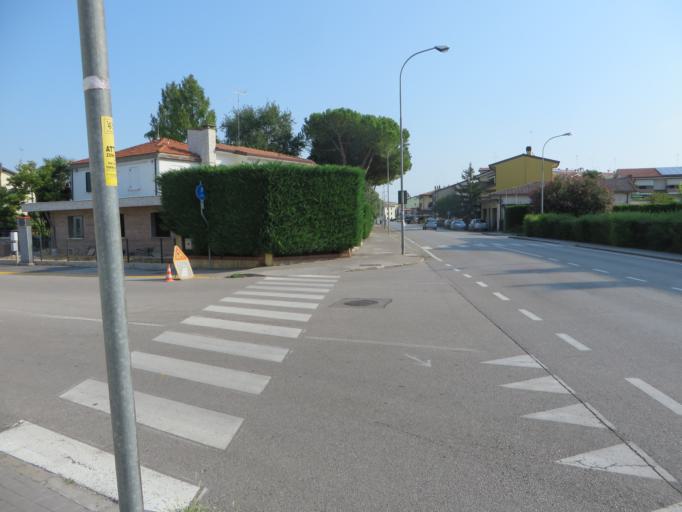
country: IT
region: Veneto
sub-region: Provincia di Venezia
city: San Dona di Piave
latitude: 45.6317
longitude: 12.5761
